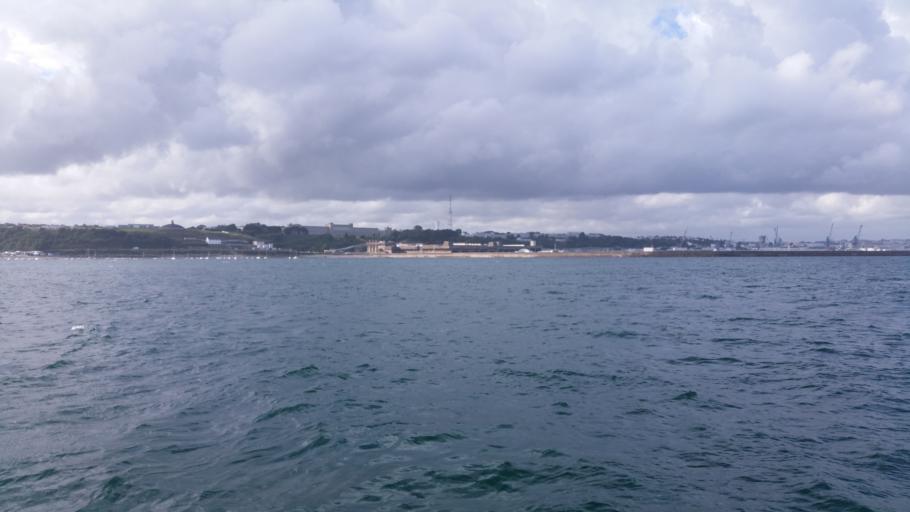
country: FR
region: Brittany
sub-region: Departement du Finistere
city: Roscanvel
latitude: 48.3544
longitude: -4.5232
